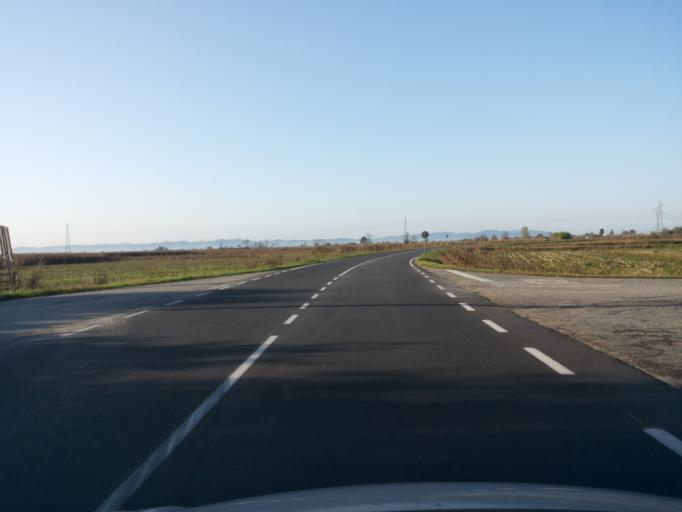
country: IT
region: Piedmont
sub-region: Provincia di Vercelli
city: Livorno Ferraris
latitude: 45.2756
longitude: 8.0890
